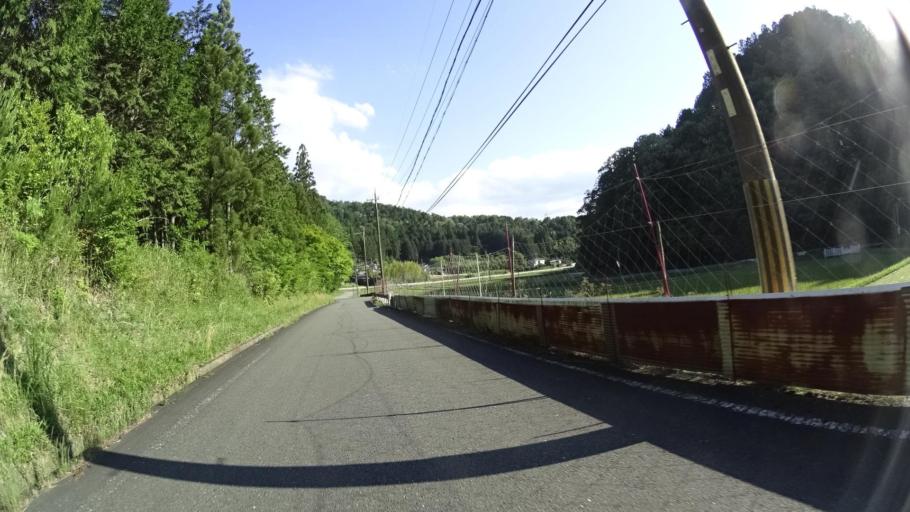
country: JP
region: Kyoto
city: Kameoka
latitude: 34.9678
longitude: 135.5628
